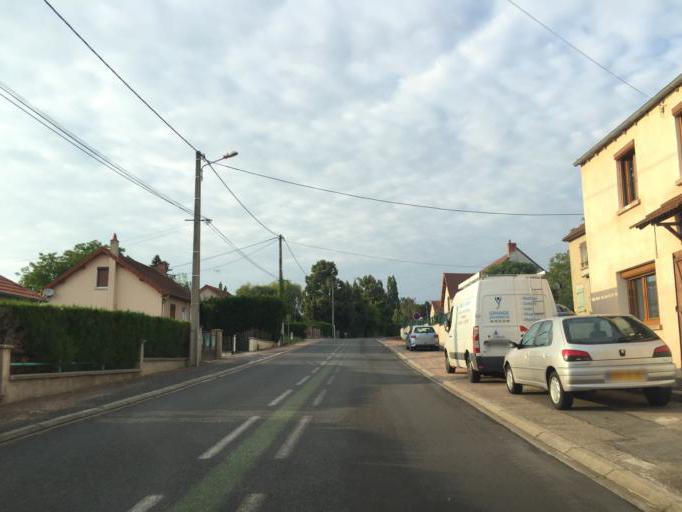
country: FR
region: Auvergne
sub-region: Departement de l'Allier
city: Saint-Germain-des-Fosses
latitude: 46.2184
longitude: 3.4327
